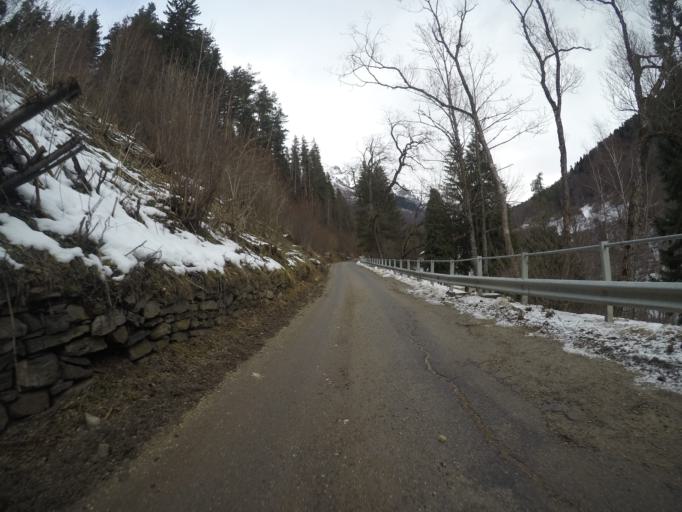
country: BG
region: Kyustendil
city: Sapareva Banya
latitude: 42.1344
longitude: 23.3414
